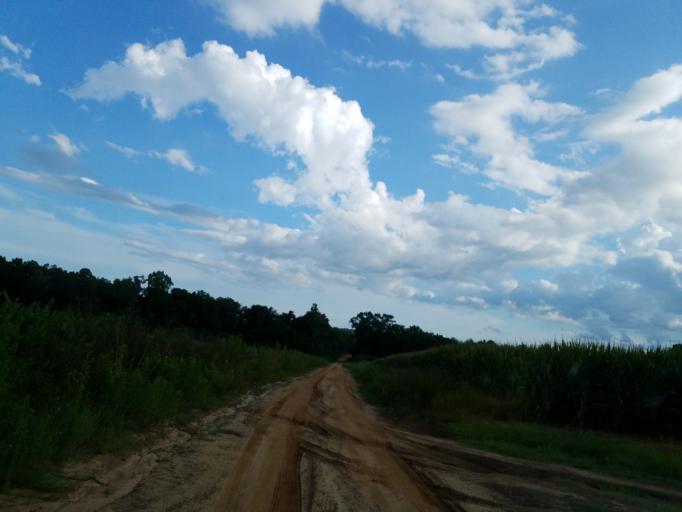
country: US
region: Georgia
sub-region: Turner County
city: Ashburn
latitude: 31.7391
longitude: -83.6609
